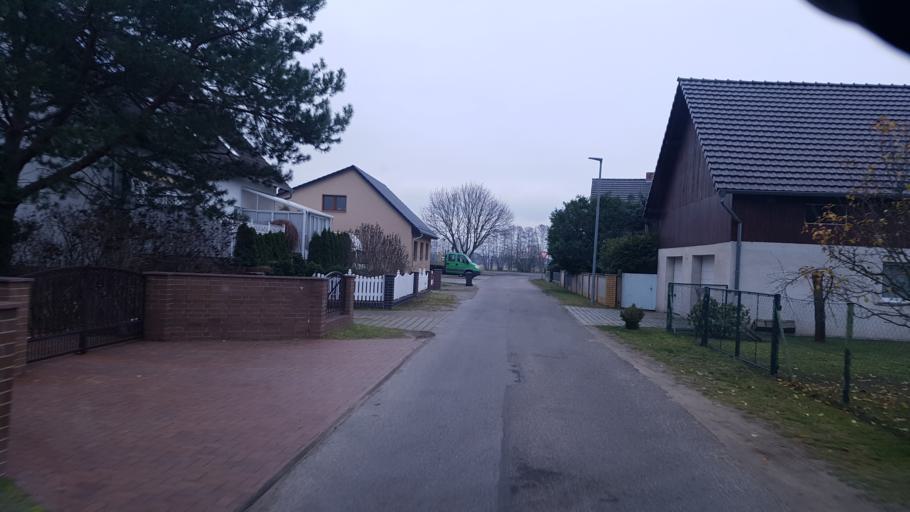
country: DE
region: Brandenburg
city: Peitz
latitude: 51.8840
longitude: 14.4213
